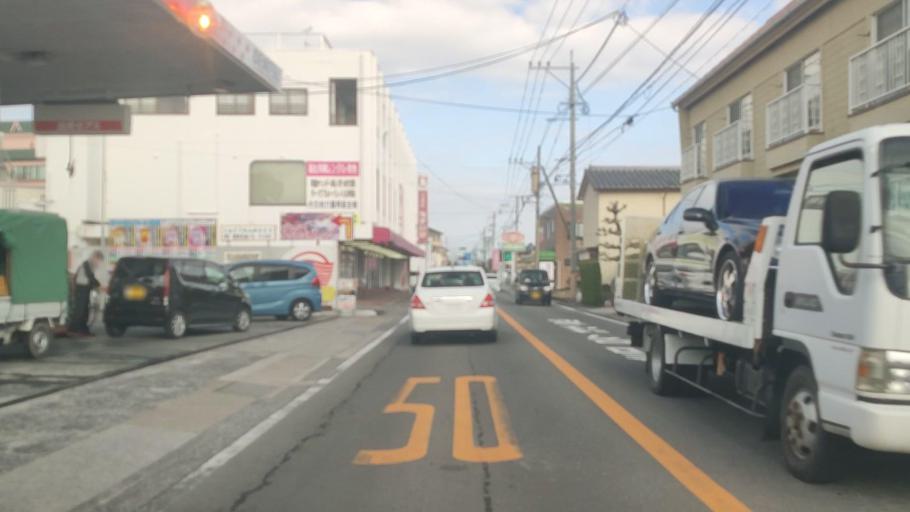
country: JP
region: Nagasaki
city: Shimabara
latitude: 32.7172
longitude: 130.3510
